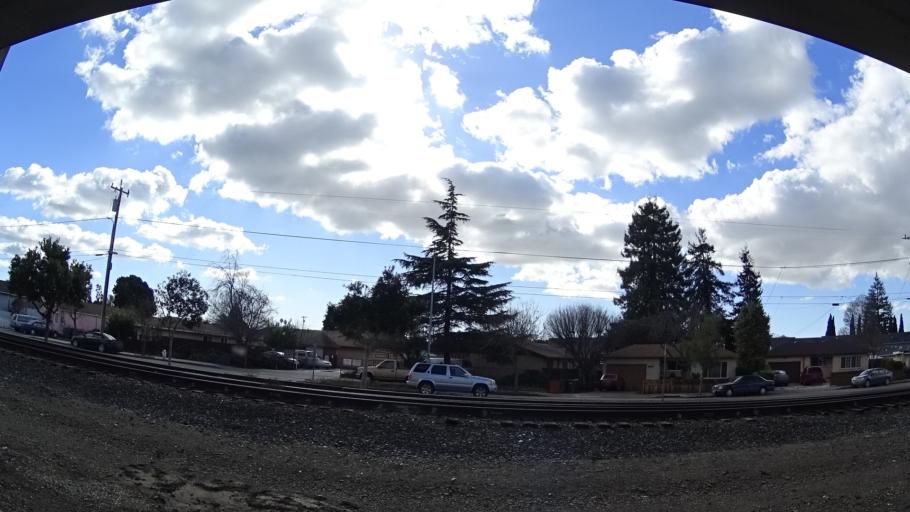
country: US
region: California
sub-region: Alameda County
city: Cherryland
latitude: 37.6789
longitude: -122.1005
